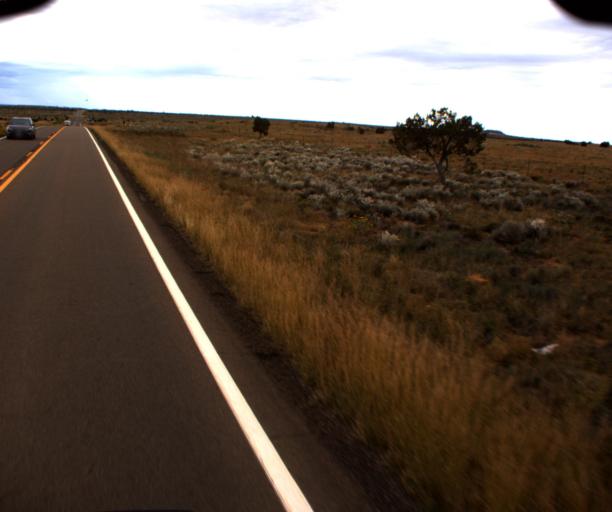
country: US
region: Arizona
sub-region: Navajo County
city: Snowflake
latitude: 34.6006
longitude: -110.0883
